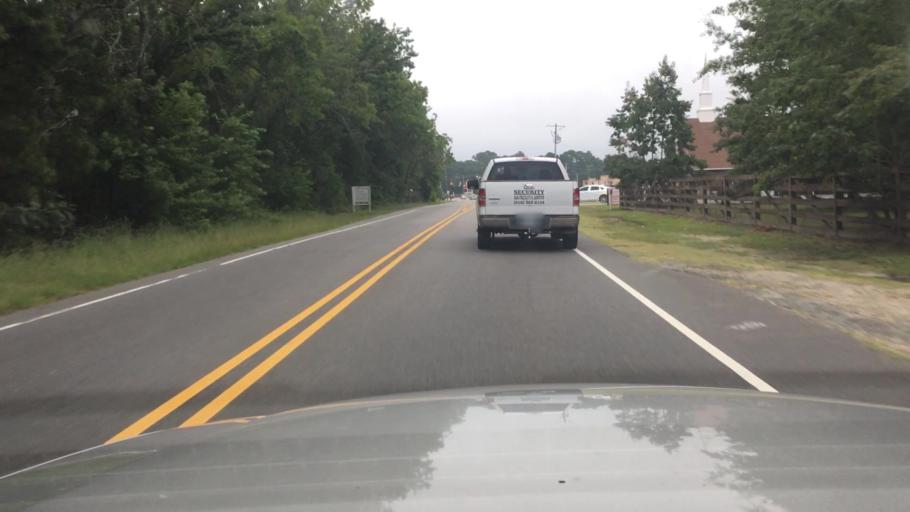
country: US
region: North Carolina
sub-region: Cumberland County
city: Hope Mills
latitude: 34.9765
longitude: -78.9895
